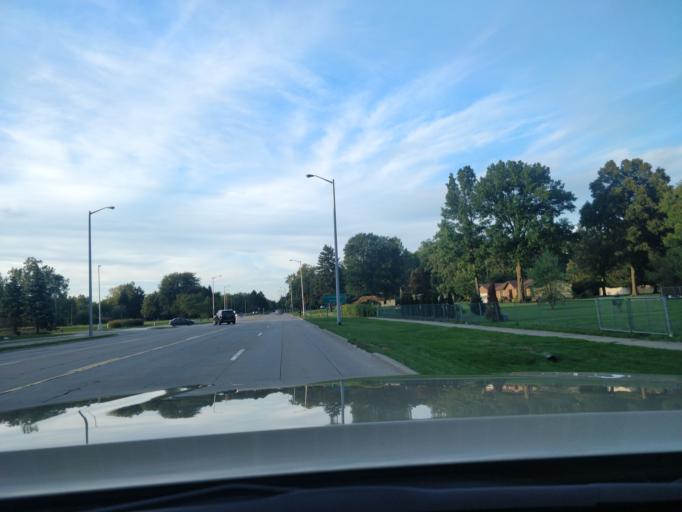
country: US
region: Michigan
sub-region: Wayne County
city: Taylor
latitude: 42.2010
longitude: -83.2481
